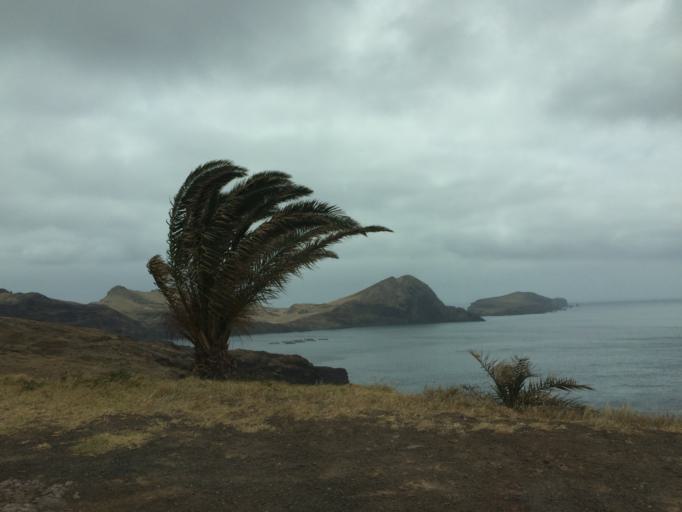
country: PT
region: Madeira
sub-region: Machico
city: Canical
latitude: 32.7408
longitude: -16.7031
